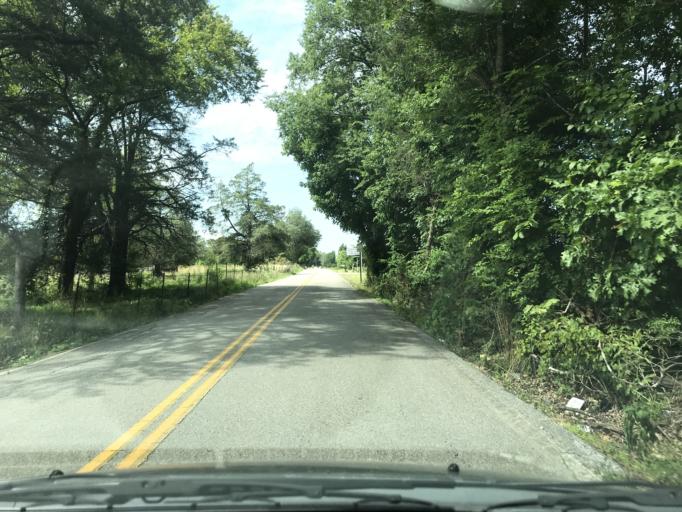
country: US
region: Tennessee
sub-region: Hamilton County
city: Lakesite
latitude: 35.1883
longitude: -85.0364
